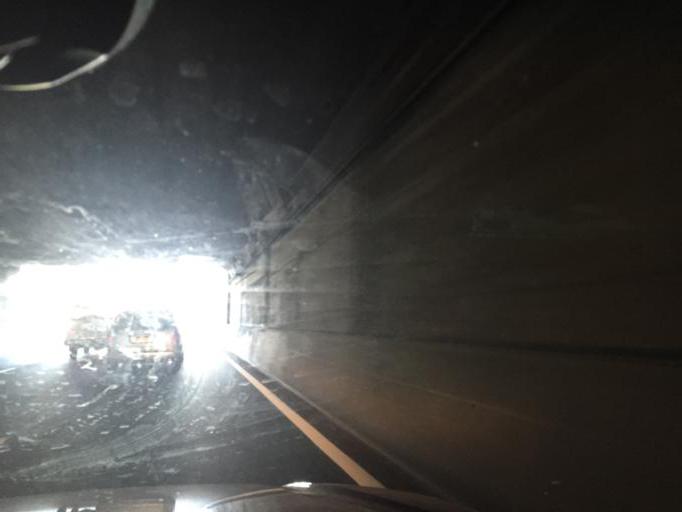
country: US
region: New York
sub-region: Queens County
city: Long Island City
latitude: 40.7487
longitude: -73.8962
